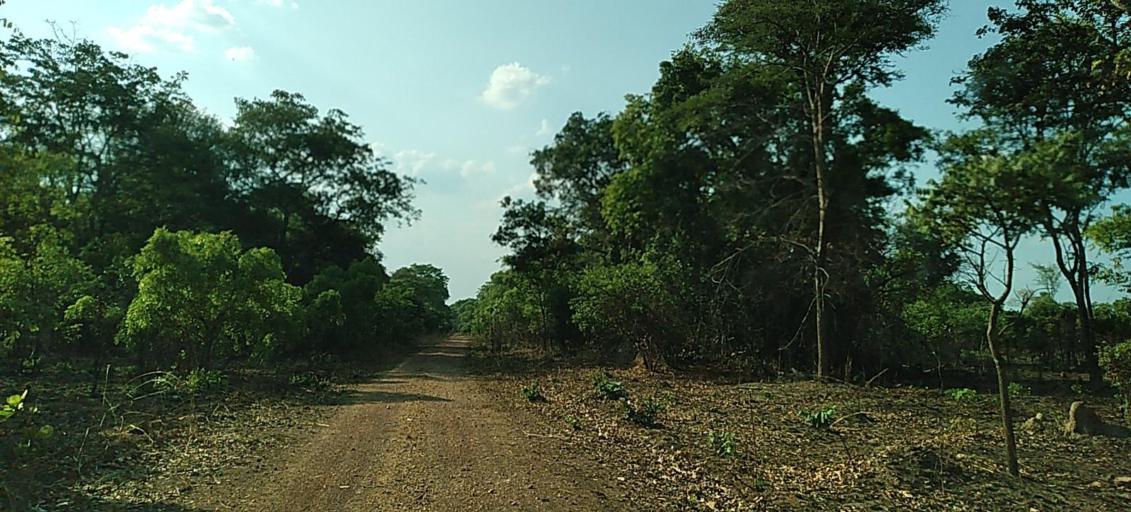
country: ZM
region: Copperbelt
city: Mpongwe
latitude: -13.3930
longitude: 28.0148
